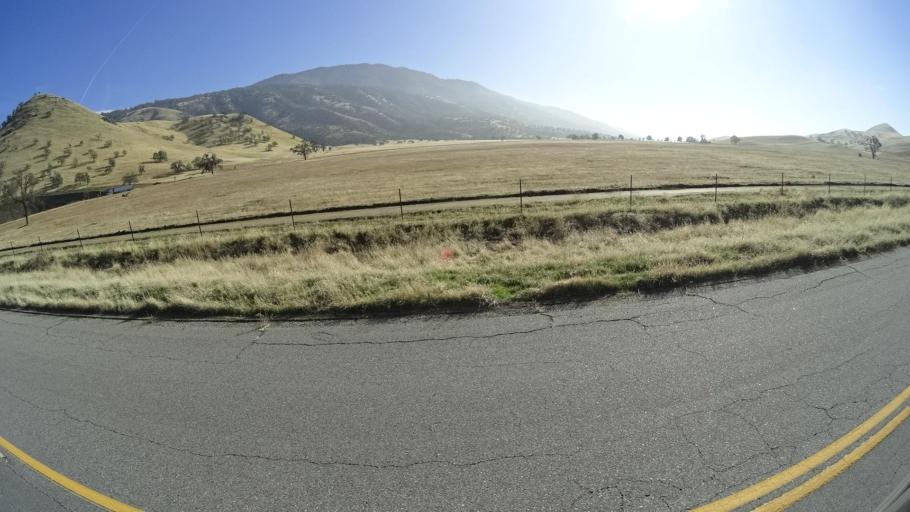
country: US
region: California
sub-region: Kern County
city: Bear Valley Springs
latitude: 35.2644
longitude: -118.6620
